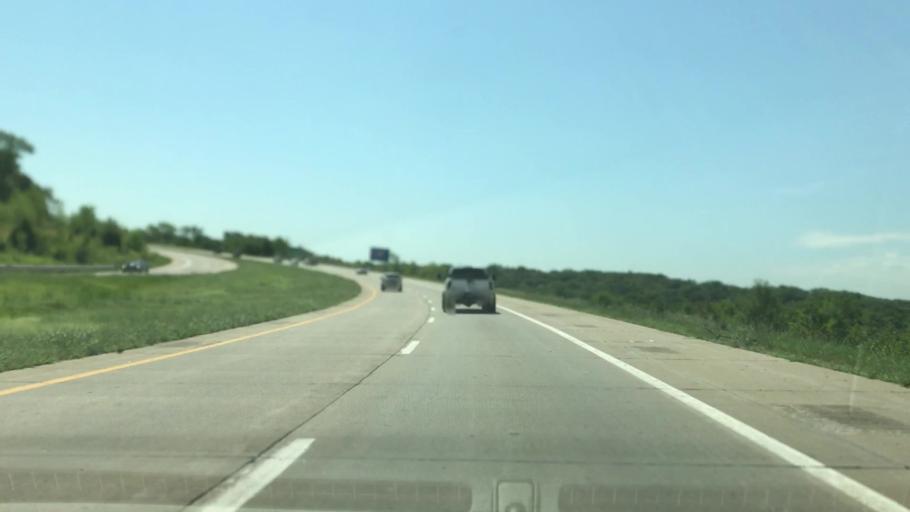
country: US
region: Missouri
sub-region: Jackson County
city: Grandview
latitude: 38.8658
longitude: -94.6004
